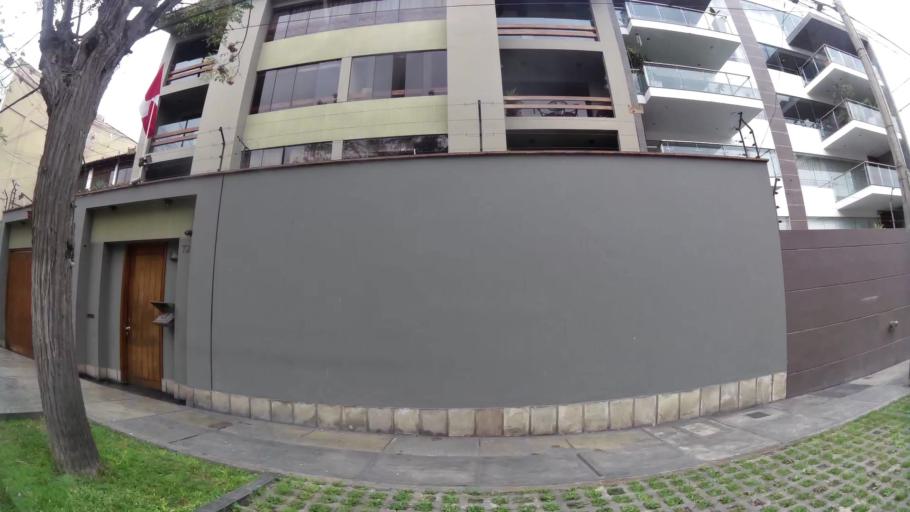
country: PE
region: Lima
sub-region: Lima
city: Surco
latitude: -12.1186
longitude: -76.9826
